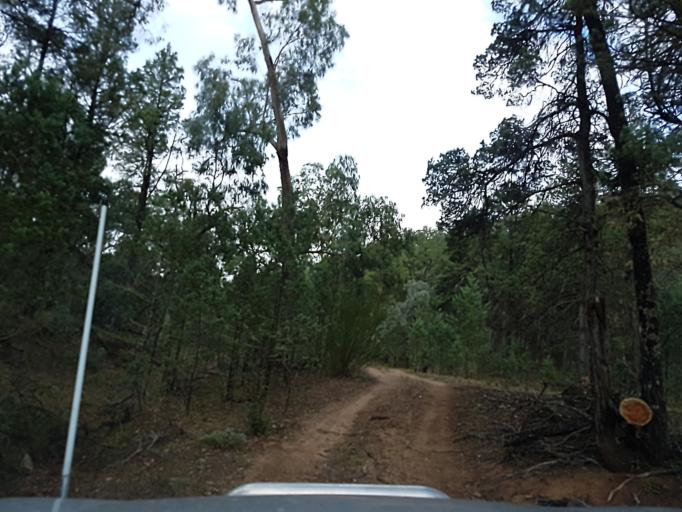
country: AU
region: New South Wales
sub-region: Snowy River
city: Jindabyne
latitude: -36.9466
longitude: 148.3817
